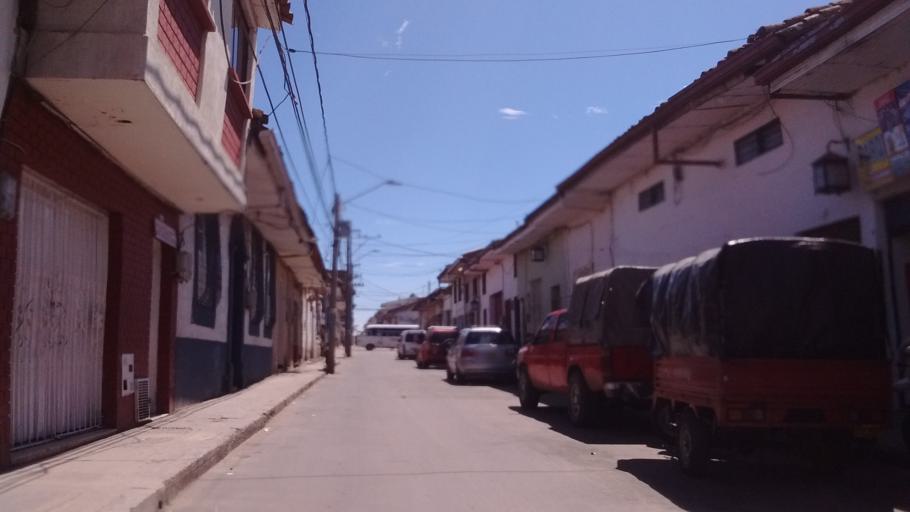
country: CO
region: Cauca
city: Popayan
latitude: 2.4378
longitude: -76.6063
